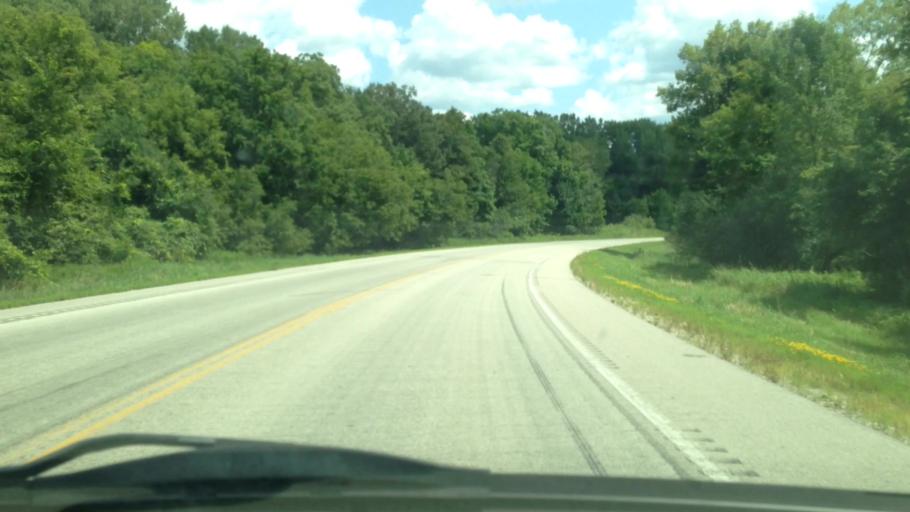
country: US
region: Minnesota
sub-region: Olmsted County
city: Rochester
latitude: 43.9765
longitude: -92.5141
